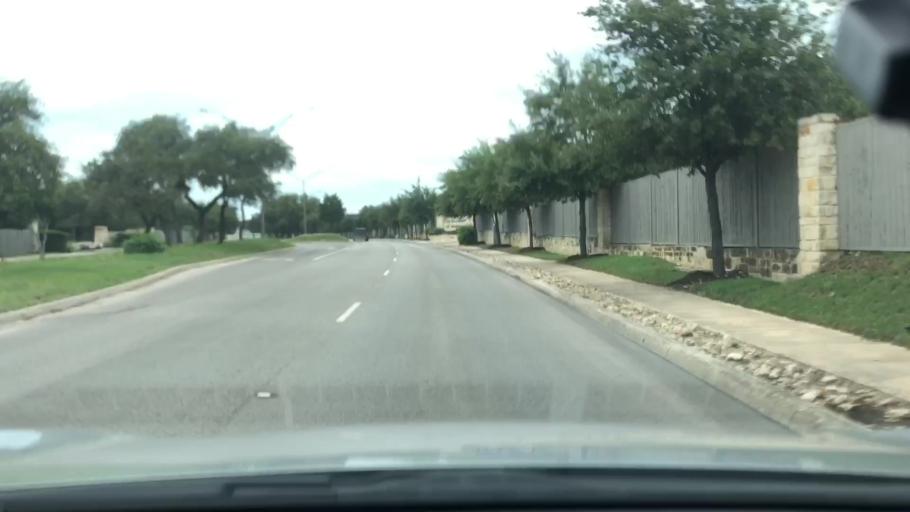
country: US
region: Texas
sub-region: Bexar County
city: Leon Valley
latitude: 29.4558
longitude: -98.6689
